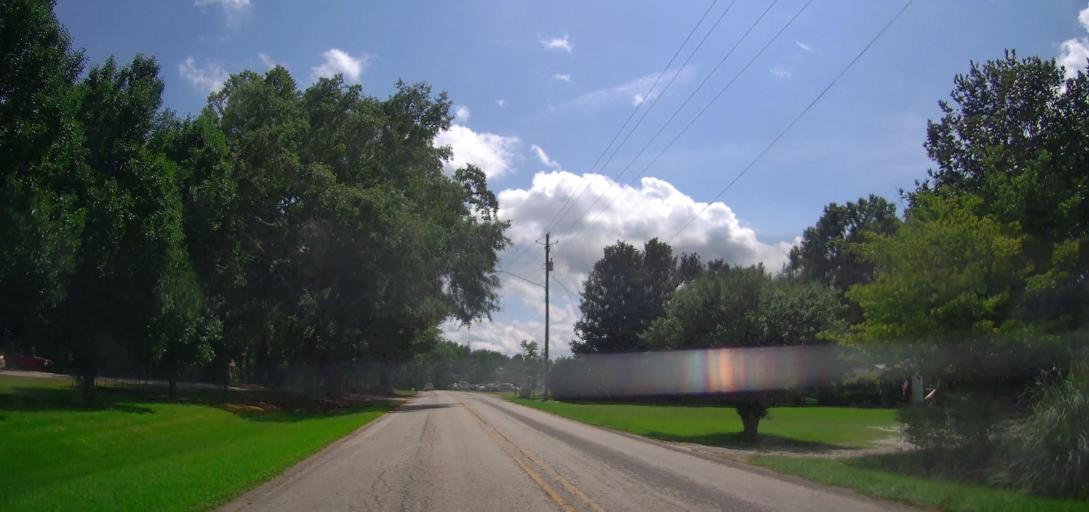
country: US
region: Georgia
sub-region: Carroll County
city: Bowdon
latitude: 33.5201
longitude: -85.3452
